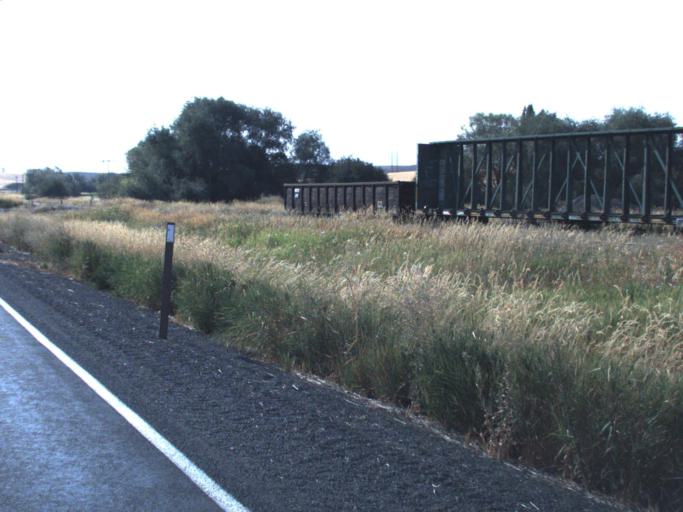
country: US
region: Washington
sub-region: Whitman County
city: Colfax
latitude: 47.0052
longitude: -117.1330
